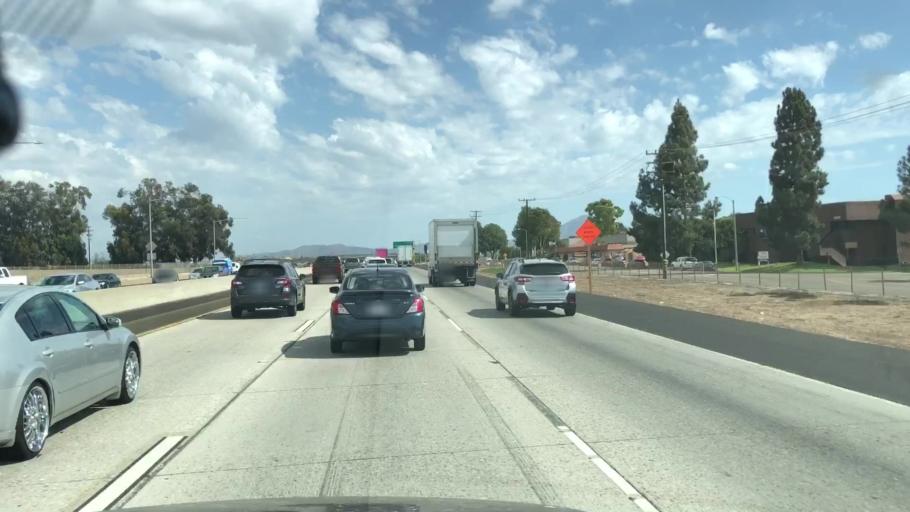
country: US
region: California
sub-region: Ventura County
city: Camarillo
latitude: 34.2206
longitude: -119.0945
